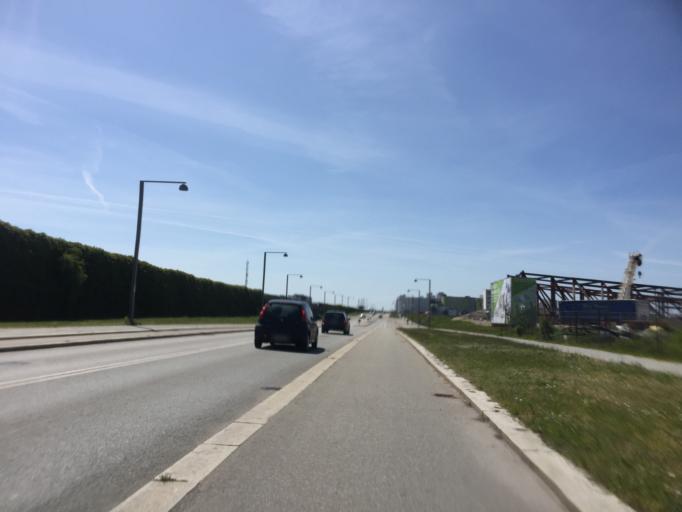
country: DK
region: Capital Region
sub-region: Tarnby Kommune
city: Tarnby
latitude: 55.6254
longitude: 12.5775
